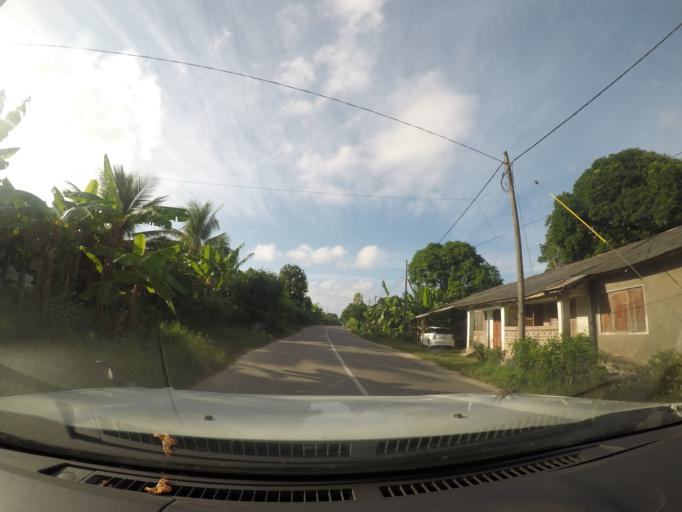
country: TZ
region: Pemba South
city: Chake Chake
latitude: -5.2462
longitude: 39.7826
